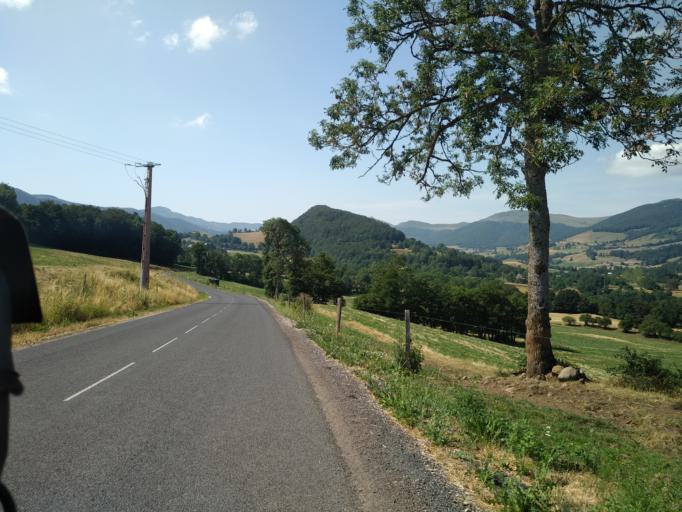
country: FR
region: Auvergne
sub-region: Departement du Cantal
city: Riom-es-Montagnes
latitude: 45.1944
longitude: 2.7161
